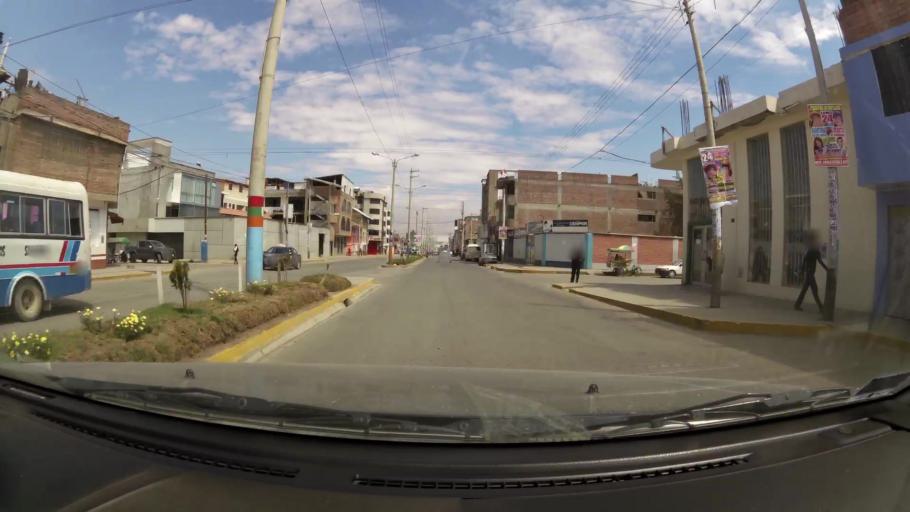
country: PE
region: Junin
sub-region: Provincia de Huancayo
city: Huancayo
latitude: -12.0827
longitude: -75.2025
